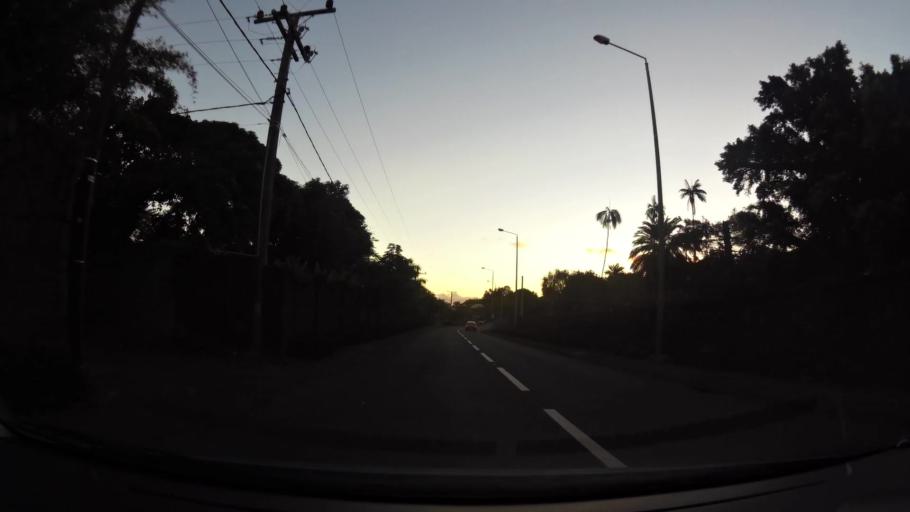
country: MU
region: Moka
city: Saint Pierre
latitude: -20.2239
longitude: 57.5152
